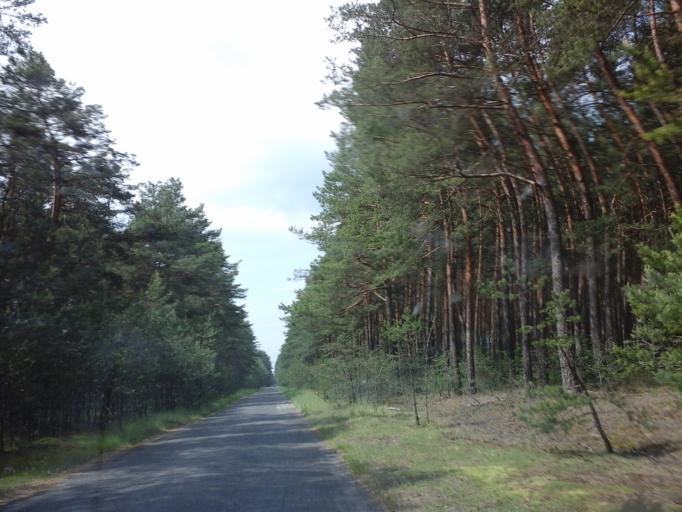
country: PL
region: West Pomeranian Voivodeship
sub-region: Powiat drawski
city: Kalisz Pomorski
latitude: 53.2018
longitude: 15.9256
